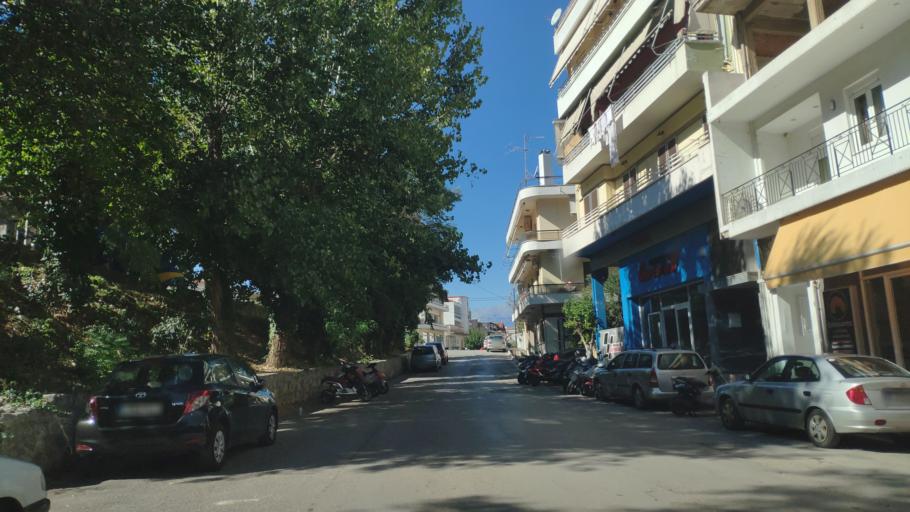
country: GR
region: Central Greece
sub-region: Nomos Voiotias
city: Livadeia
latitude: 38.4390
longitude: 22.8716
